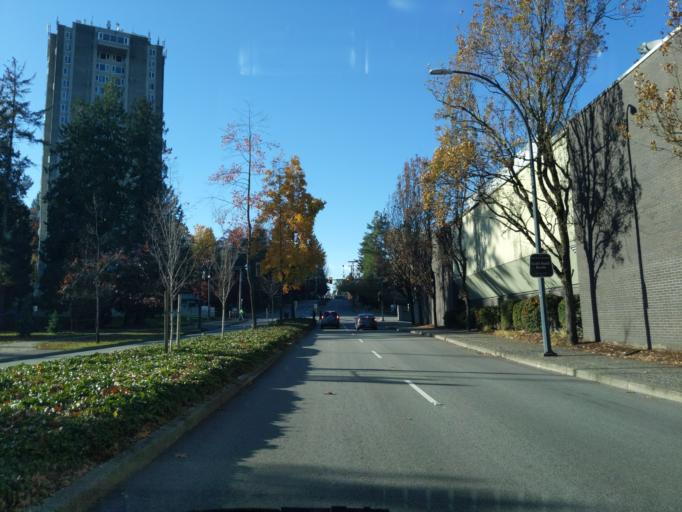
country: CA
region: British Columbia
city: New Westminster
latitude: 49.1857
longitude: -122.8508
